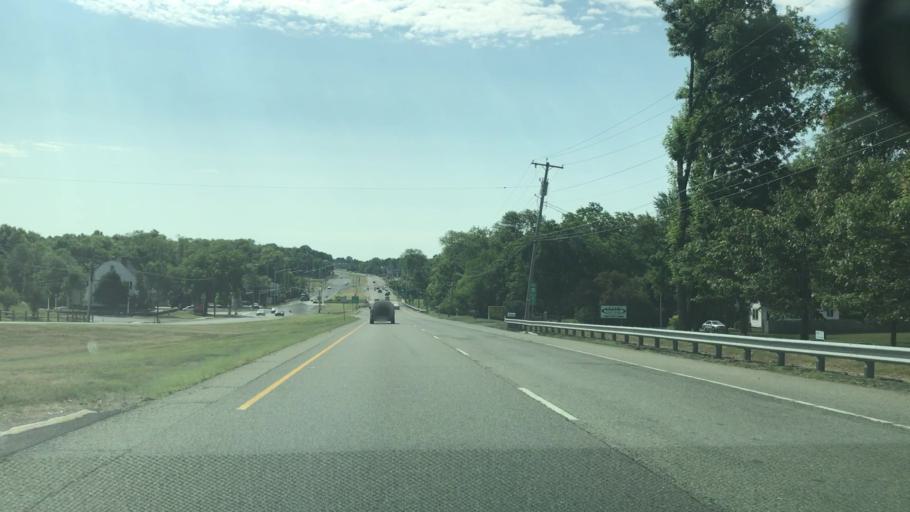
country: US
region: New Jersey
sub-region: Hunterdon County
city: Whitehouse Station
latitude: 40.6251
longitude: -74.7701
